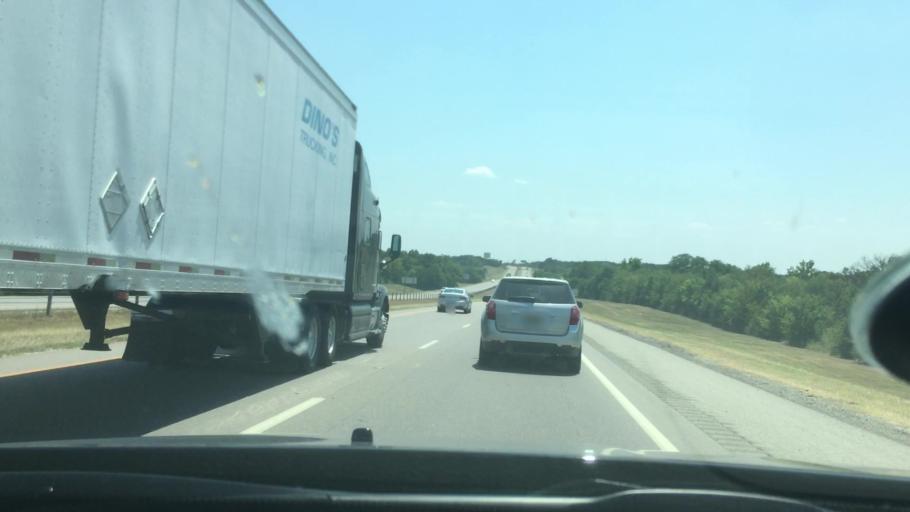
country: US
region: Oklahoma
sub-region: Bryan County
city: Durant
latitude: 33.9945
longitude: -96.4068
